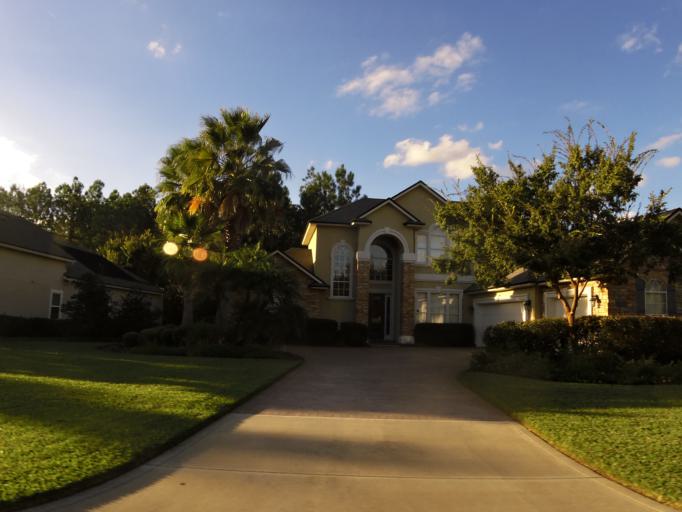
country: US
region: Florida
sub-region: Saint Johns County
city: Fruit Cove
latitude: 30.0619
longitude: -81.6414
